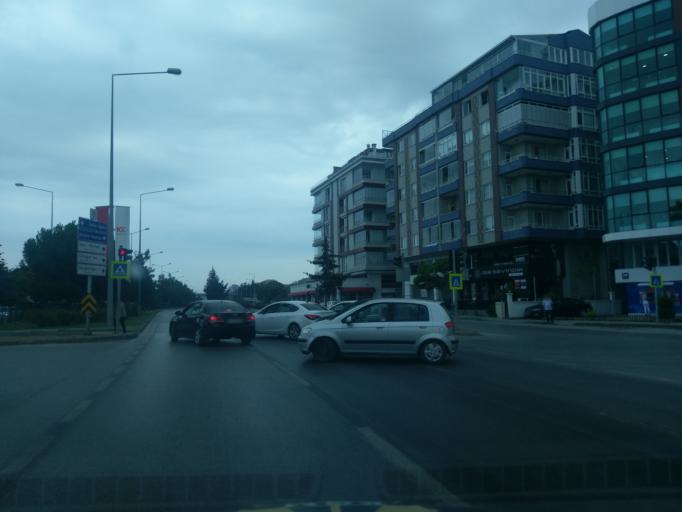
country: TR
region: Samsun
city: Samsun
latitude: 41.3327
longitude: 36.2839
